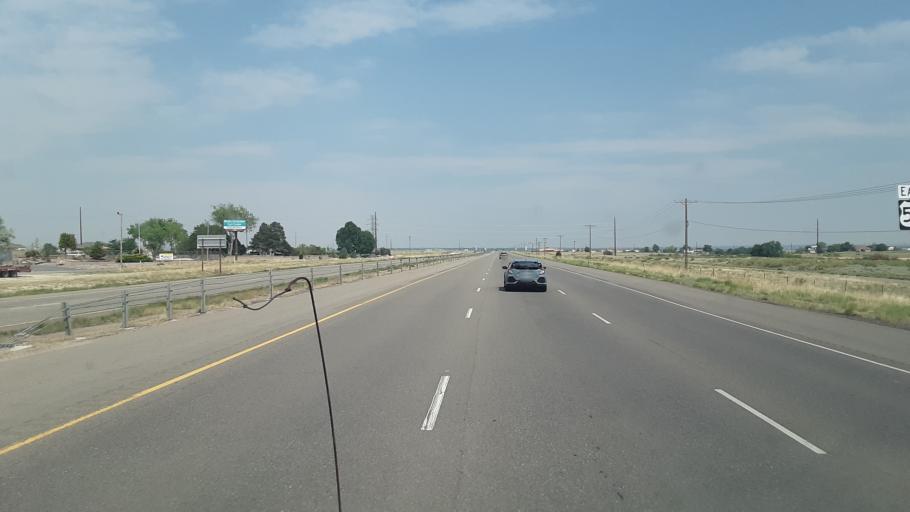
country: US
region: Colorado
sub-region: Pueblo County
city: Pueblo West
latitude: 38.3225
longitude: -104.6962
